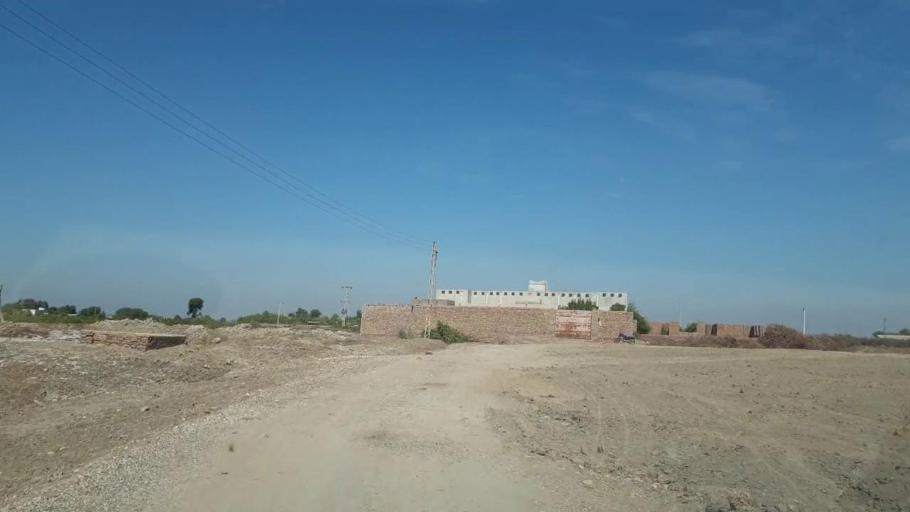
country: PK
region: Sindh
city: Pithoro
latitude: 25.6310
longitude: 69.2480
